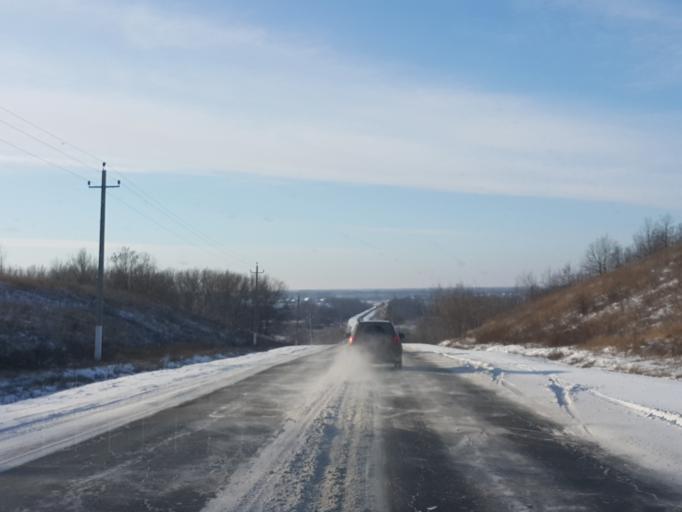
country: RU
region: Tambov
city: Znamenka
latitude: 52.4177
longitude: 41.4886
